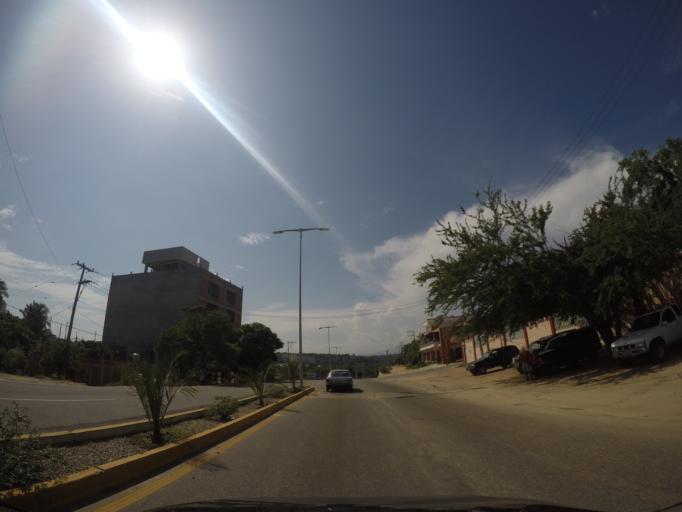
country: MX
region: Oaxaca
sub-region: San Pedro Mixtepec -Dto. 22 -
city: Puerto Escondido
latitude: 15.8586
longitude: -97.0576
